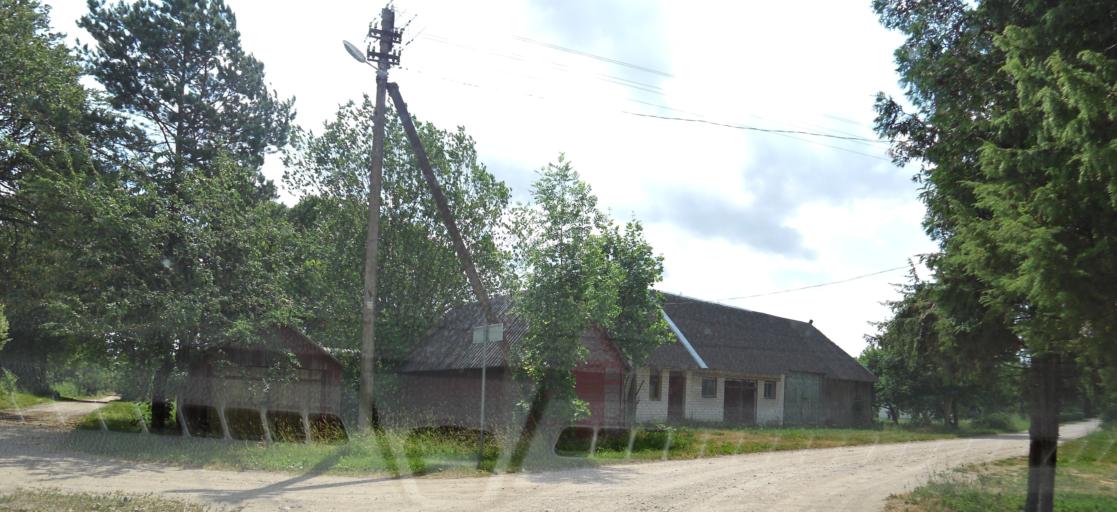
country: LT
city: Obeliai
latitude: 56.1086
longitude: 25.0081
